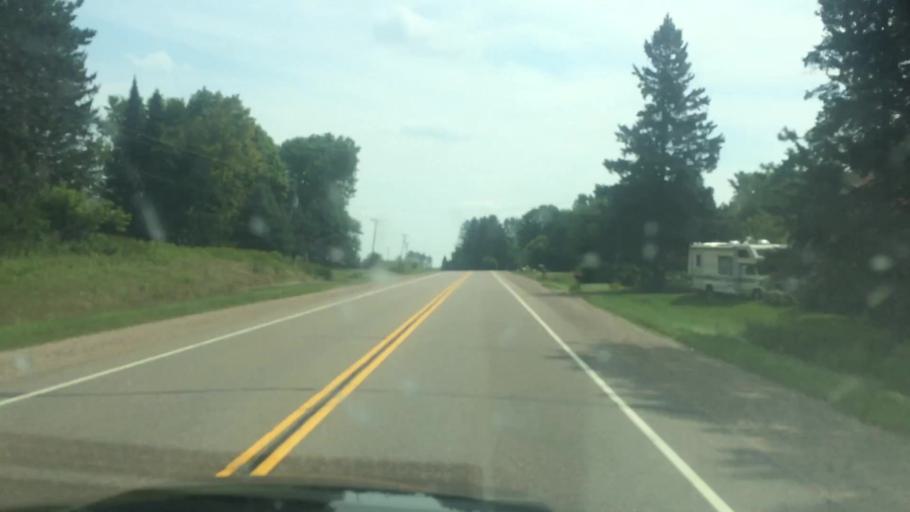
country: US
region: Wisconsin
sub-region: Langlade County
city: Antigo
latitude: 45.1692
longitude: -88.9806
